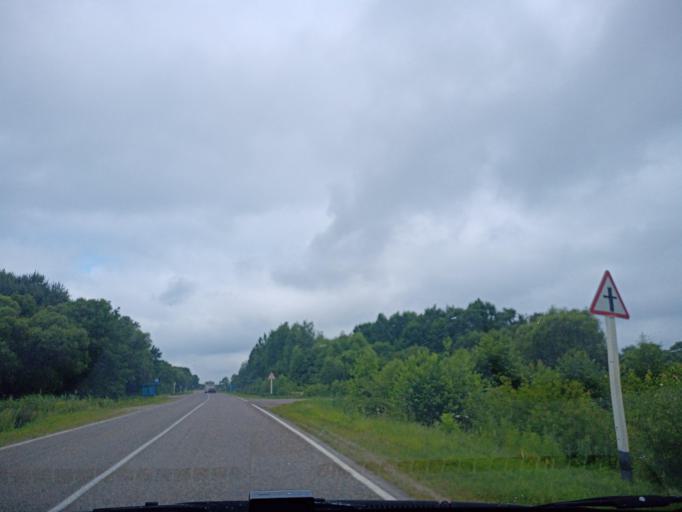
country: RU
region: Primorskiy
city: Novopokrovka
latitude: 45.9710
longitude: 134.2332
